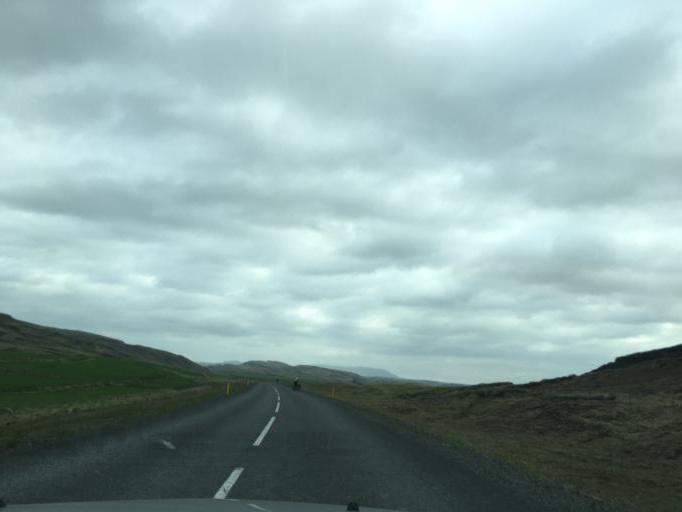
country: IS
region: South
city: Vestmannaeyjar
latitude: 64.2302
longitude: -20.2461
